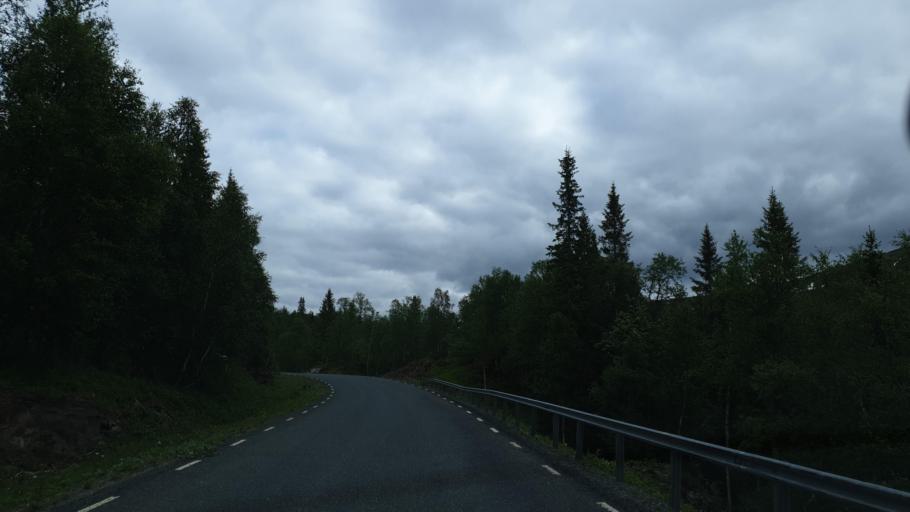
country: NO
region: Nordland
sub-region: Hattfjelldal
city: Hattfjelldal
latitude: 65.4289
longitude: 14.5973
